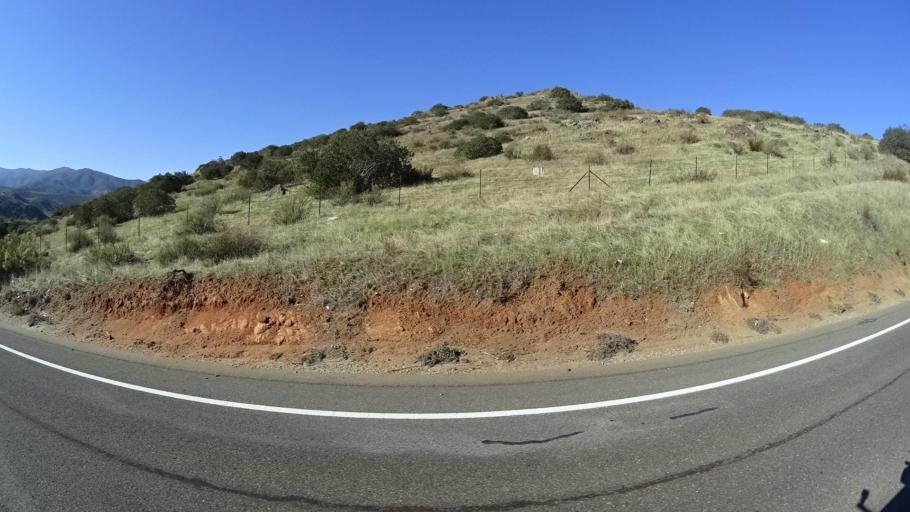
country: US
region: California
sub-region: San Diego County
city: Jamul
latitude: 32.6745
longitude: -116.8364
